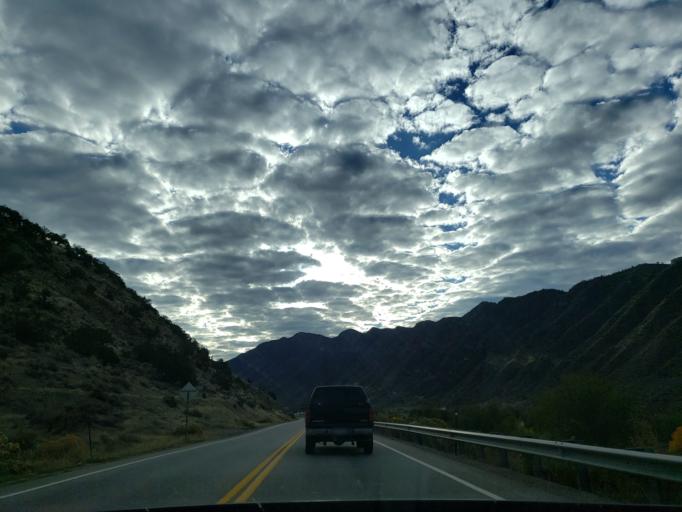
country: US
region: Colorado
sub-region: Garfield County
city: New Castle
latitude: 39.5703
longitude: -107.5228
